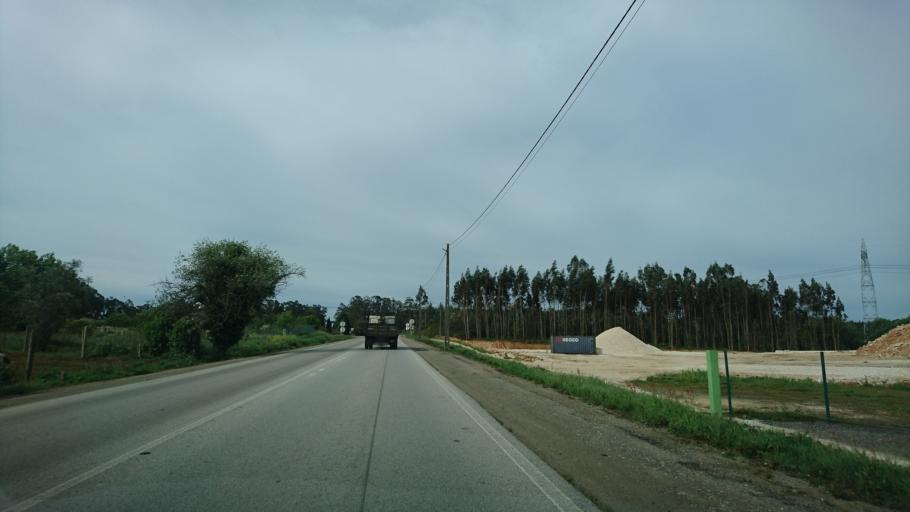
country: PT
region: Aveiro
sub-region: Albergaria-A-Velha
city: Albergaria-a-Velha
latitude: 40.6957
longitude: -8.5132
